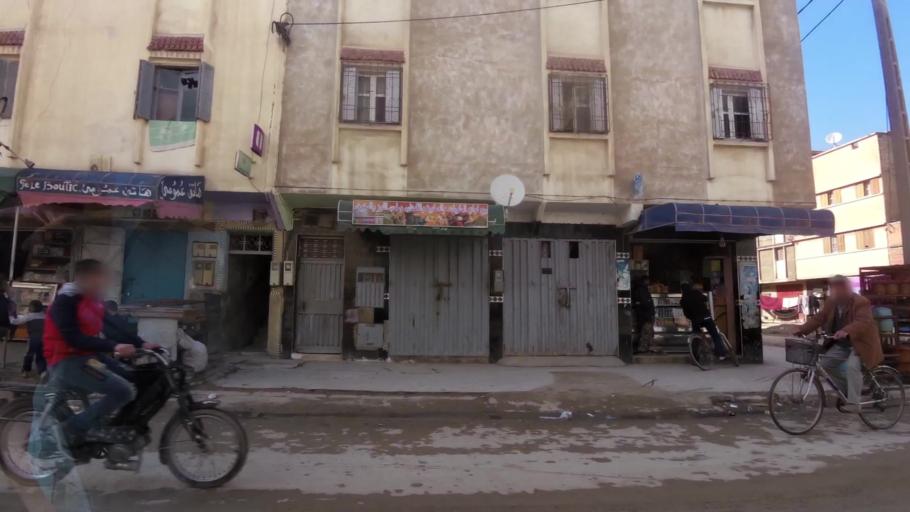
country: MA
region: Chaouia-Ouardigha
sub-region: Settat Province
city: Berrechid
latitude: 33.2743
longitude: -7.5721
